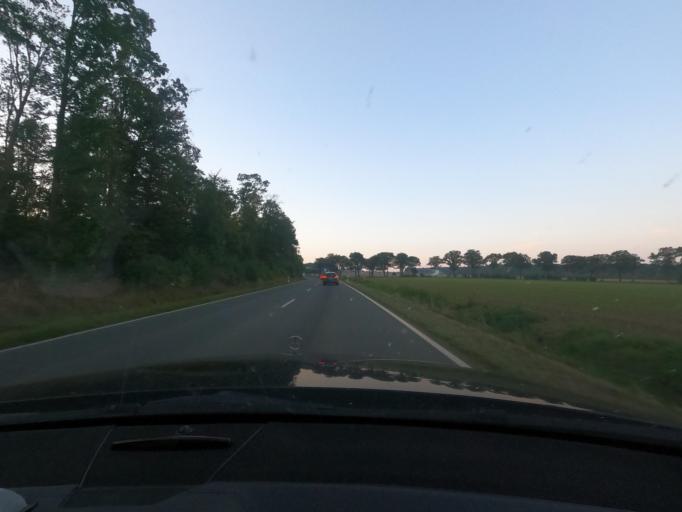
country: DE
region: North Rhine-Westphalia
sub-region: Regierungsbezirk Detmold
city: Salzkotten
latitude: 51.6196
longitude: 8.5867
